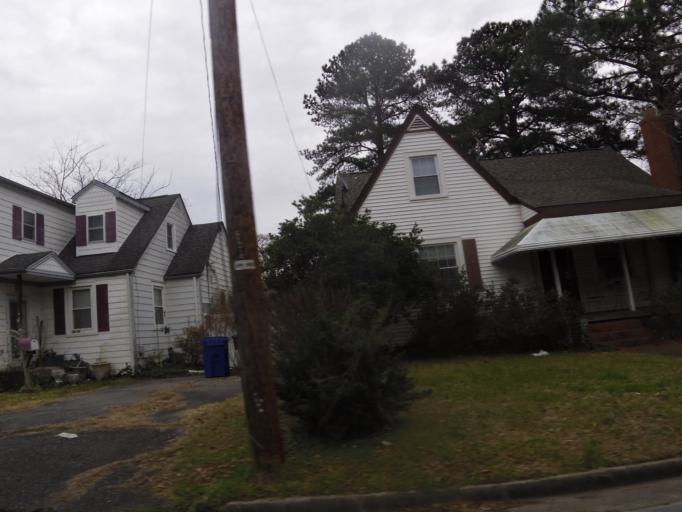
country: US
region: Virginia
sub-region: City of Portsmouth
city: Portsmouth
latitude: 36.8438
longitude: -76.3254
